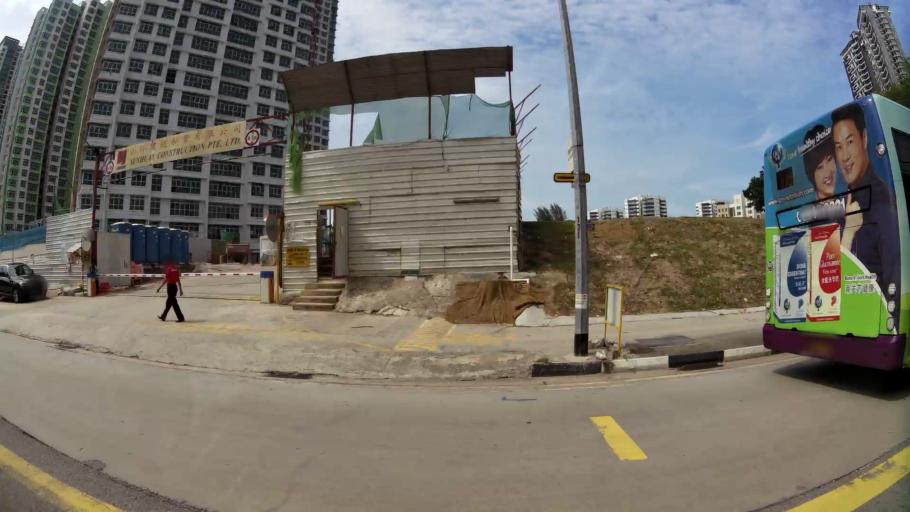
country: SG
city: Singapore
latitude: 1.3174
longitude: 103.7639
